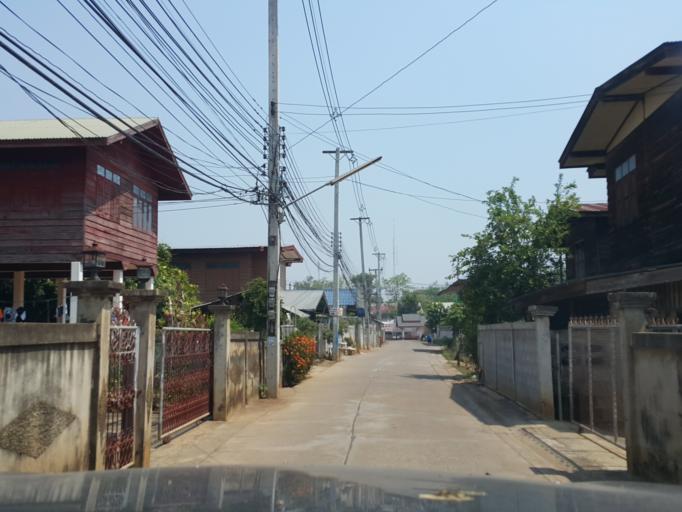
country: TH
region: Sukhothai
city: Thung Saliam
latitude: 17.3195
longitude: 99.5621
